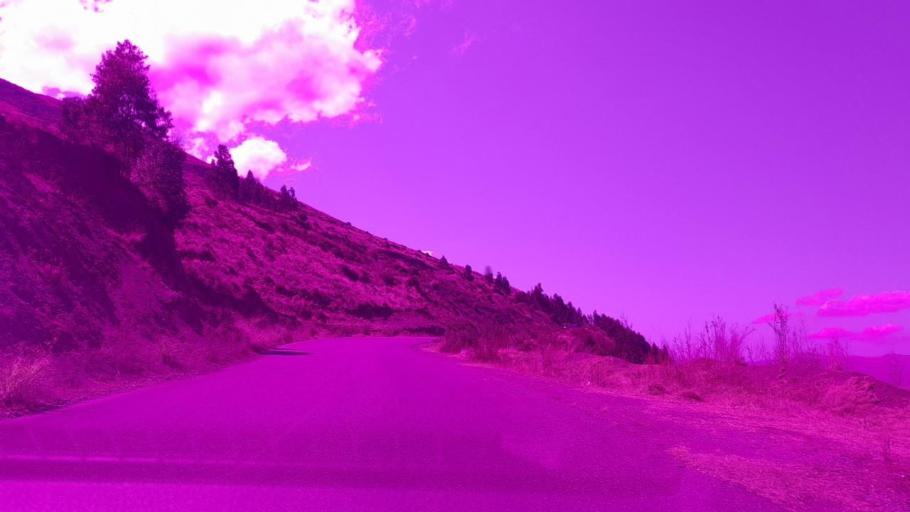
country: PE
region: Cusco
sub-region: Provincia de Cusco
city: Cusco
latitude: -13.4969
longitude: -71.9279
